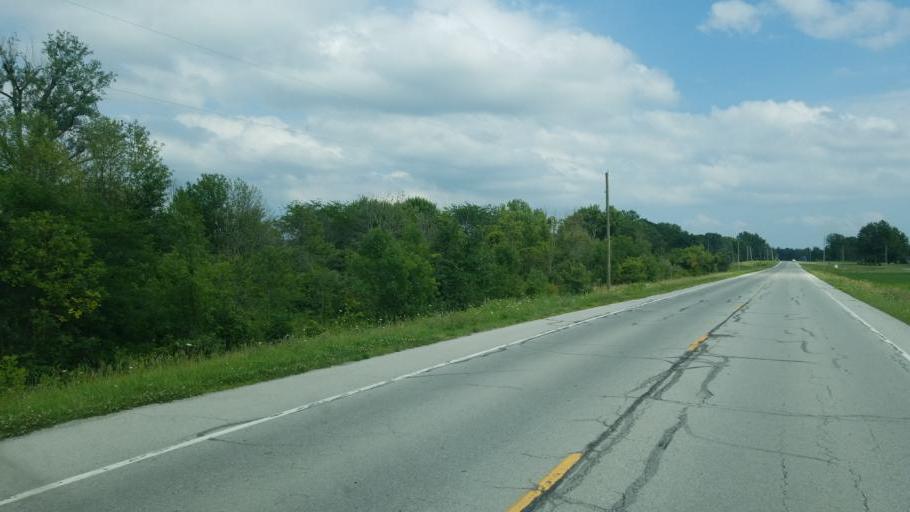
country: US
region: Ohio
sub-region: Crawford County
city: Crestline
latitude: 40.8015
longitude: -82.7671
